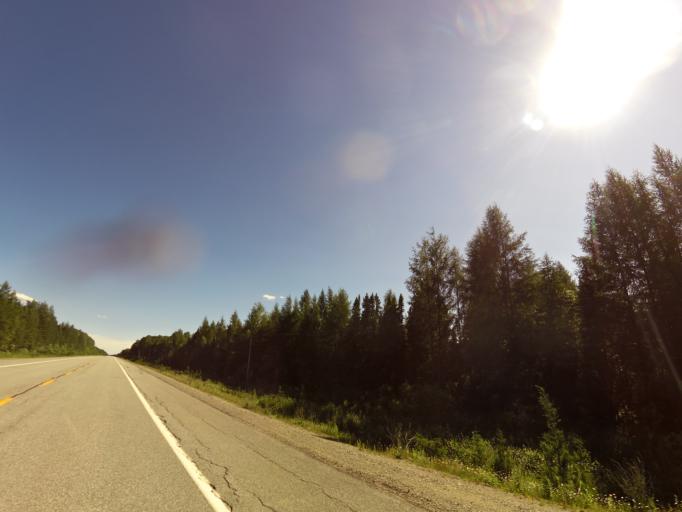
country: CA
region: Quebec
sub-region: Abitibi-Temiscamingue
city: Senneterre
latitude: 47.9682
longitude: -77.3608
